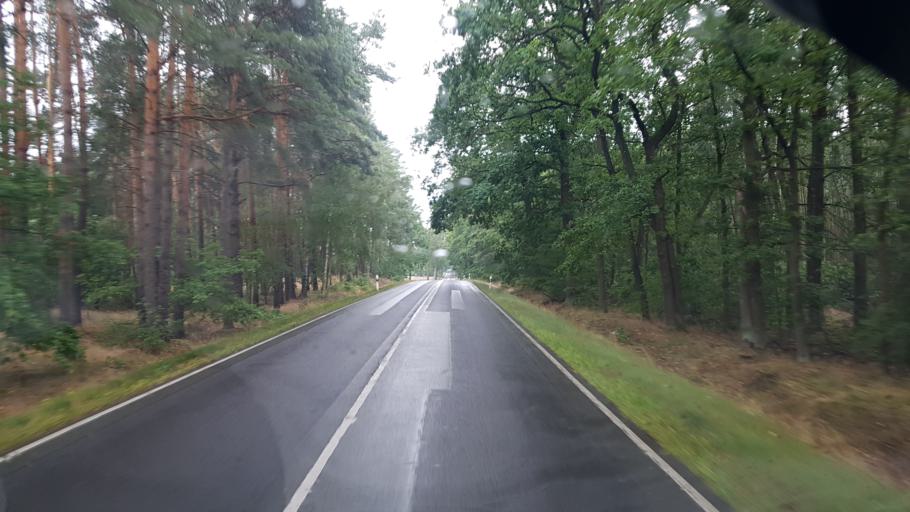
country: DE
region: Brandenburg
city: Lebusa
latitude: 51.8156
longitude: 13.4198
